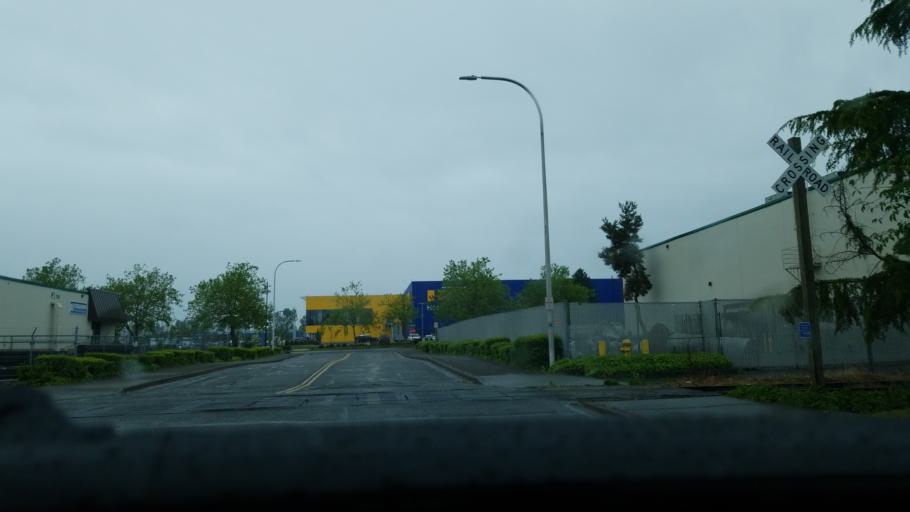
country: US
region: Washington
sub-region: King County
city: Renton
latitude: 47.4449
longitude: -122.2278
